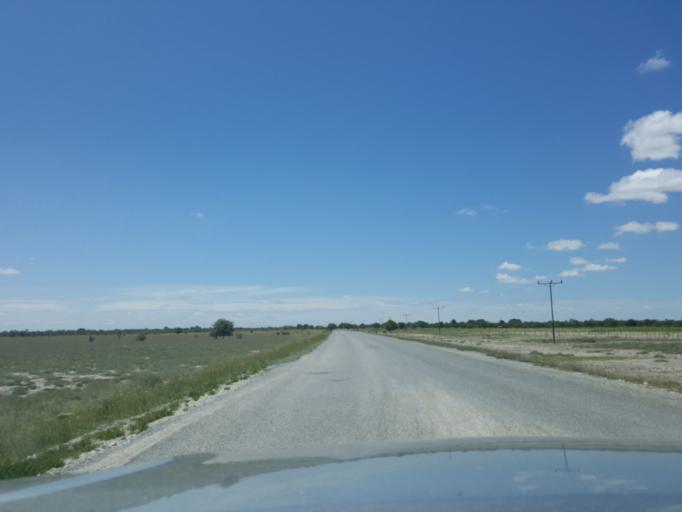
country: BW
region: Central
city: Nata
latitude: -20.1585
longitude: 25.8428
